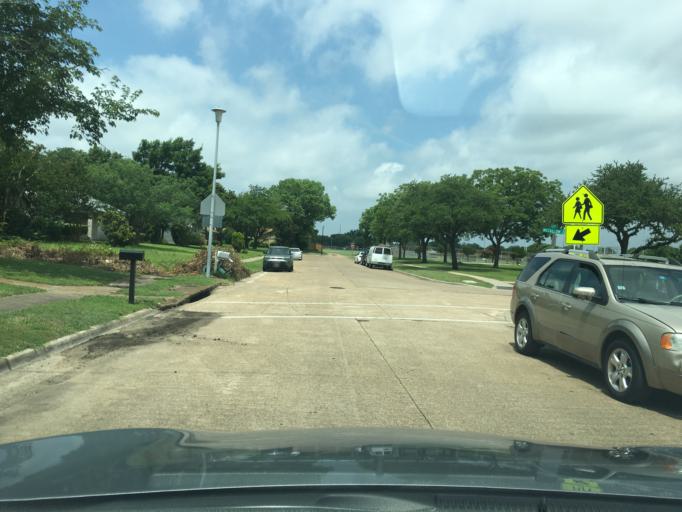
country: US
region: Texas
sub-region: Dallas County
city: Garland
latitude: 32.9258
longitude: -96.6749
